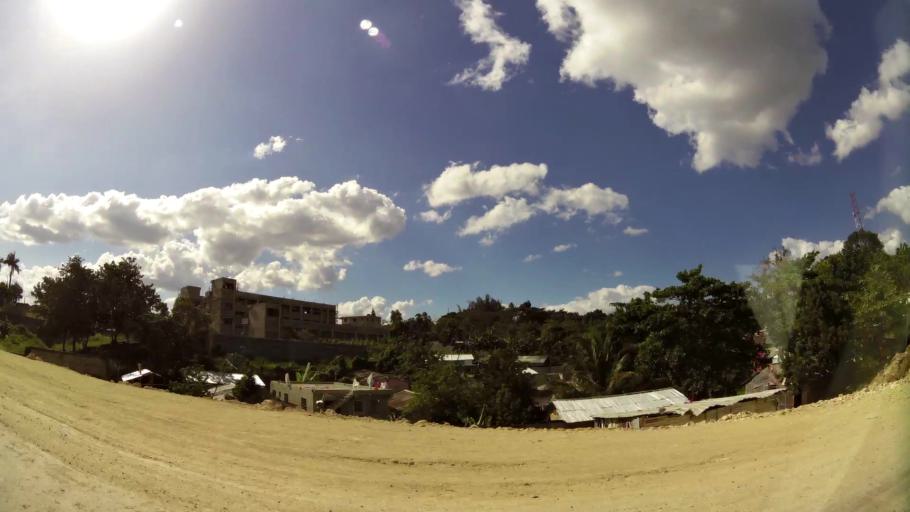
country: DO
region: Santo Domingo
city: Santo Domingo Oeste
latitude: 18.5451
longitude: -70.0425
